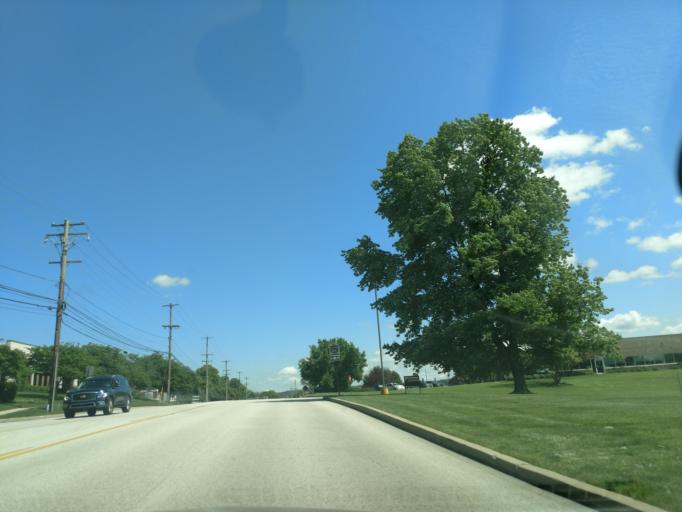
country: US
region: Pennsylvania
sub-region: Montgomery County
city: King of Prussia
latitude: 40.1003
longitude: -75.3969
